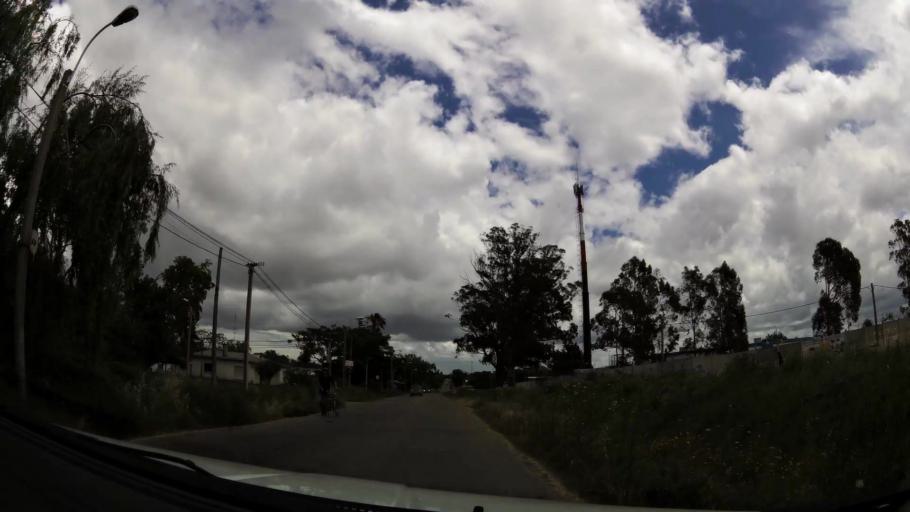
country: UY
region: Montevideo
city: Montevideo
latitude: -34.8232
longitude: -56.1657
